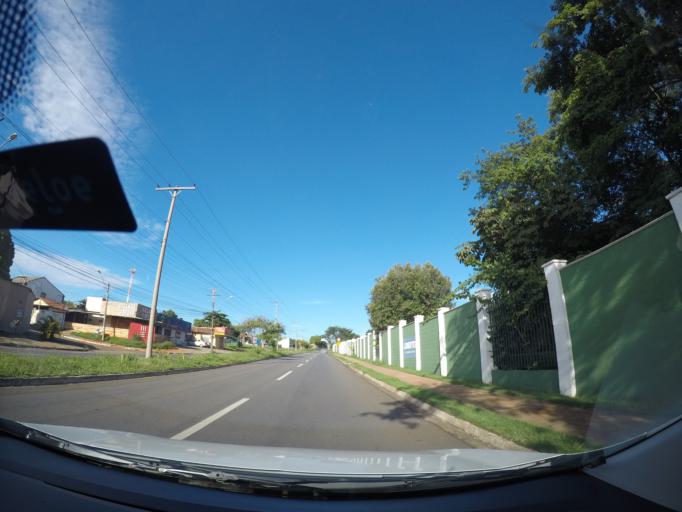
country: BR
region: Goias
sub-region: Goiania
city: Goiania
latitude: -16.7322
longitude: -49.2972
